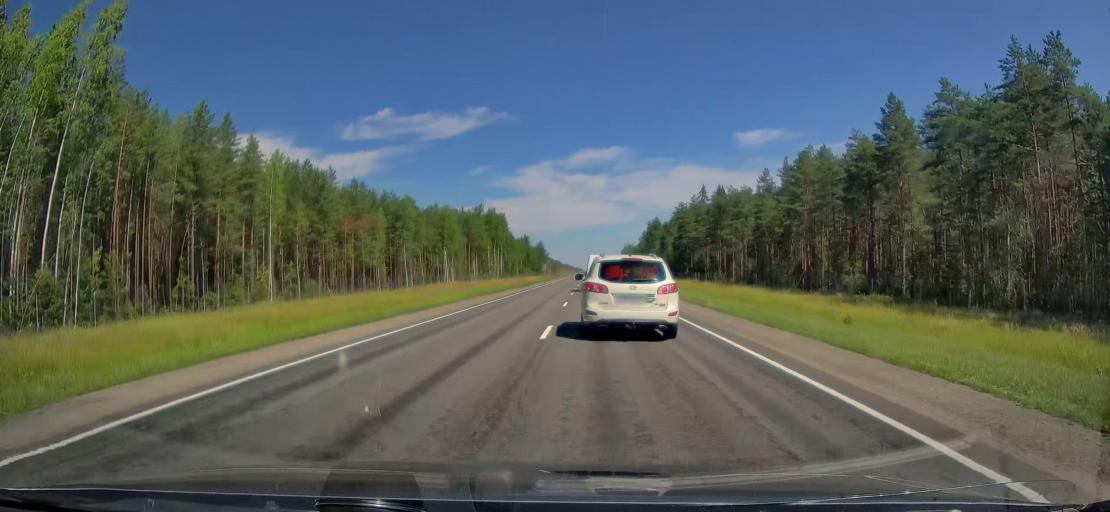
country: RU
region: Vologda
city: Khokhlovo
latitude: 58.9693
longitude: 37.3138
